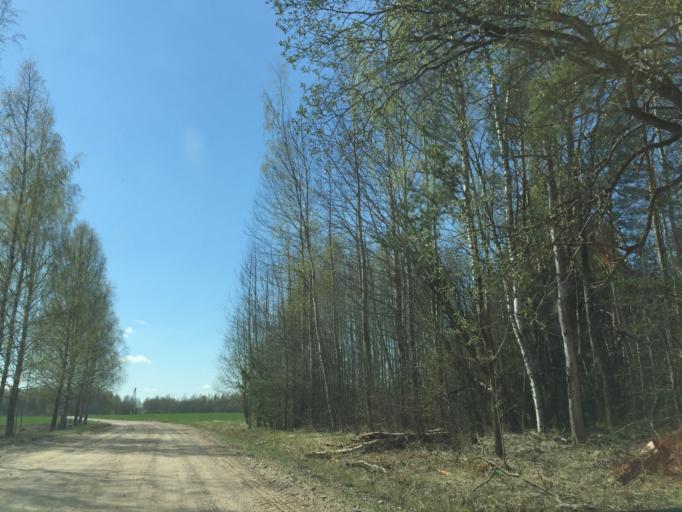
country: LV
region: Smiltene
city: Smiltene
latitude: 57.5652
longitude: 25.9077
